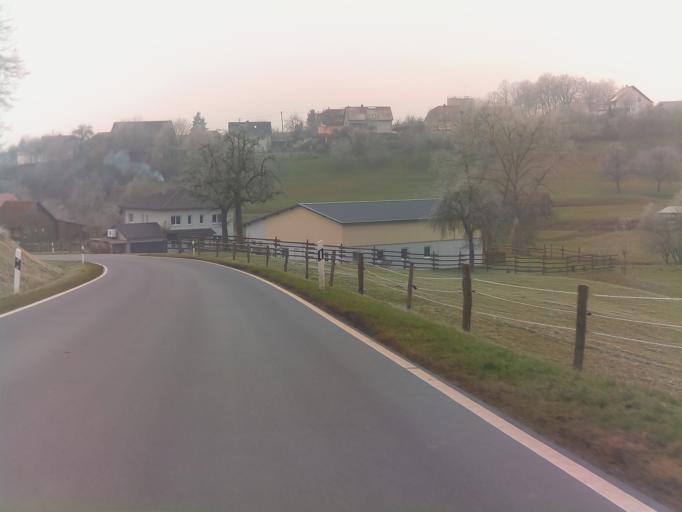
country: DE
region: Baden-Wuerttemberg
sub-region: Karlsruhe Region
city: Rosenberg
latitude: 49.4160
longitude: 9.5226
